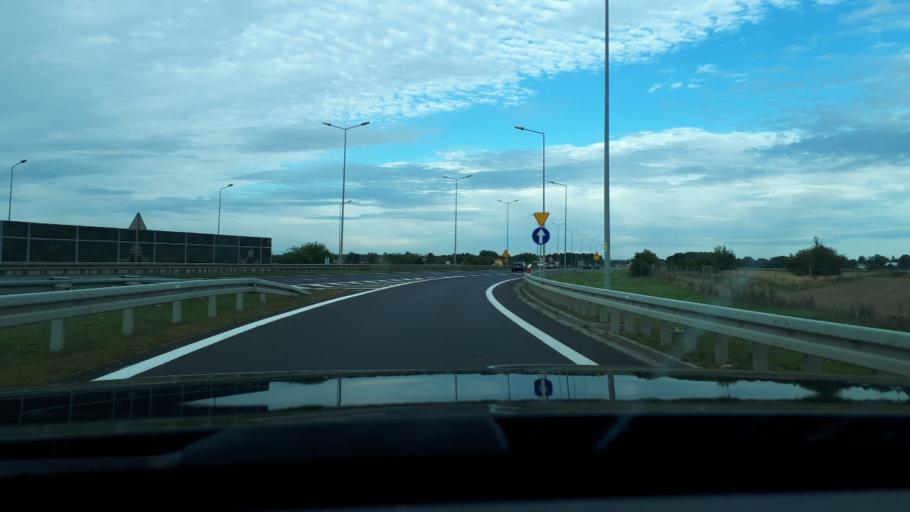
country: PL
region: Lower Silesian Voivodeship
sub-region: Powiat olesnicki
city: Olesnica
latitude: 51.2298
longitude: 17.3741
